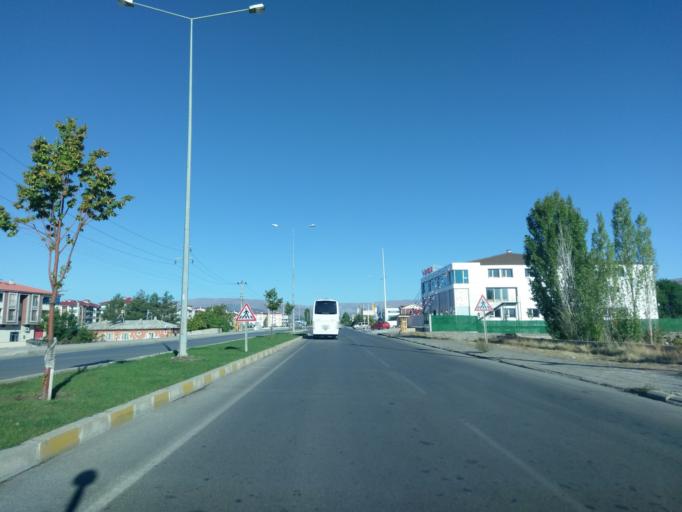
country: TR
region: Erzincan
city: Erzincan
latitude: 39.7556
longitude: 39.4501
